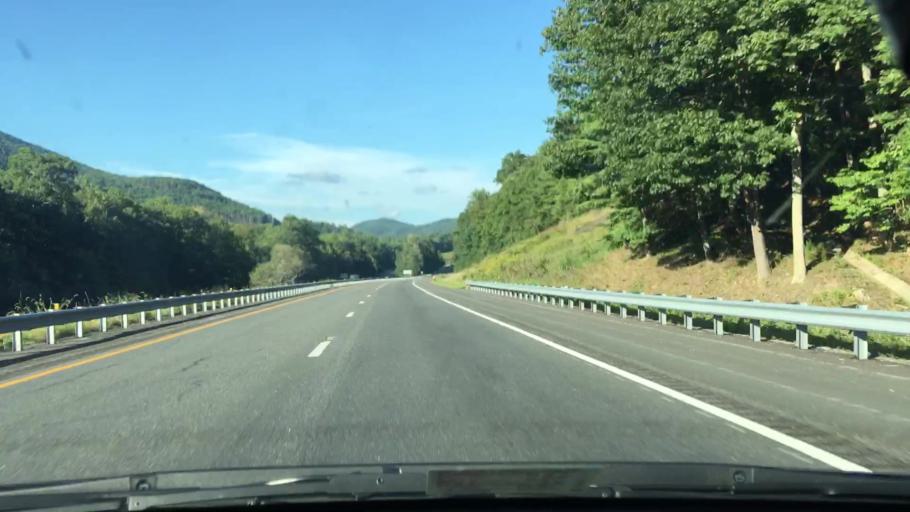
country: US
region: Virginia
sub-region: Alleghany County
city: Clifton Forge
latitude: 37.8262
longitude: -79.6591
